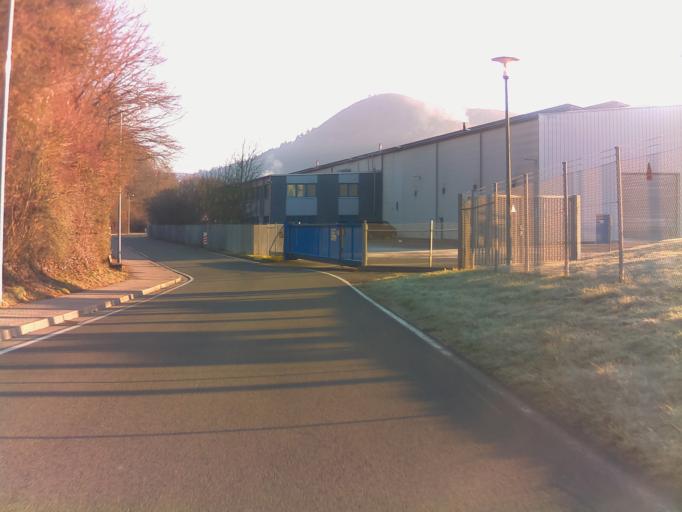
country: DE
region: Rheinland-Pfalz
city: Barenbach
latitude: 49.7684
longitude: 7.4391
